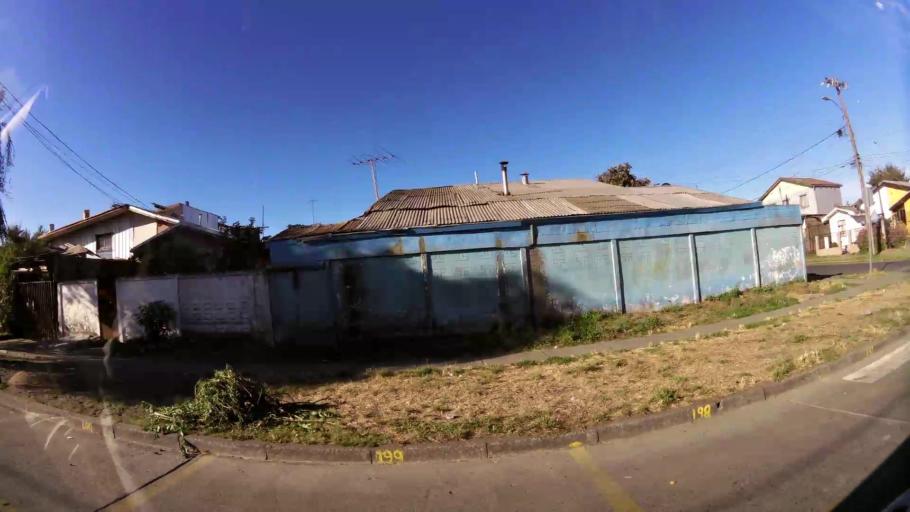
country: CL
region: Biobio
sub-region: Provincia de Concepcion
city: Concepcion
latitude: -36.8272
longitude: -73.1285
